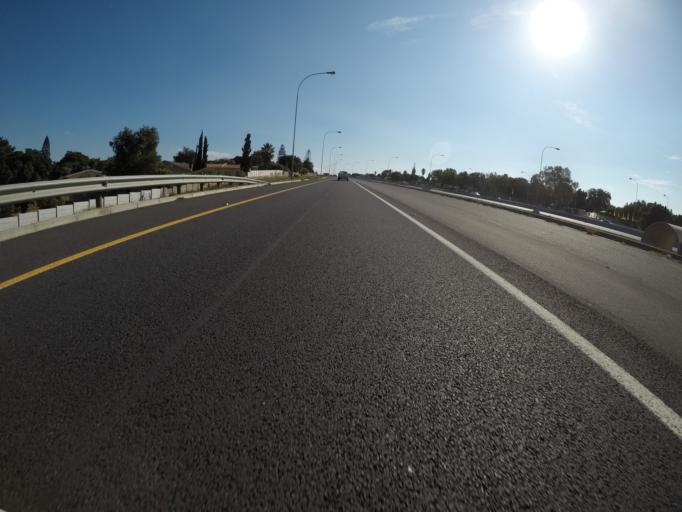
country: ZA
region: Western Cape
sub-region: City of Cape Town
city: Kraaifontein
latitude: -33.8741
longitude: 18.6667
